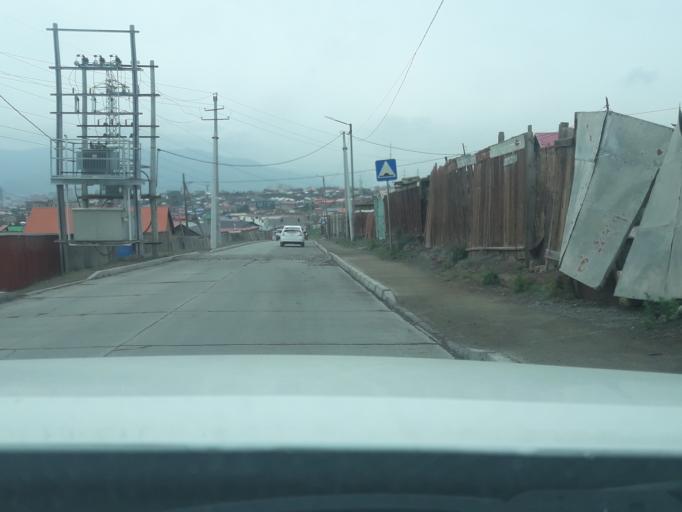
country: MN
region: Ulaanbaatar
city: Ulaanbaatar
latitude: 47.9494
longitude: 106.9049
